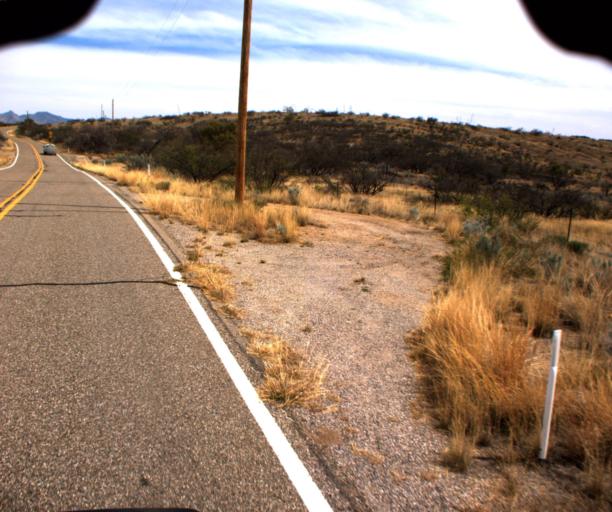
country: US
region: Arizona
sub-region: Cochise County
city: Willcox
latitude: 32.1606
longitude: -109.5705
